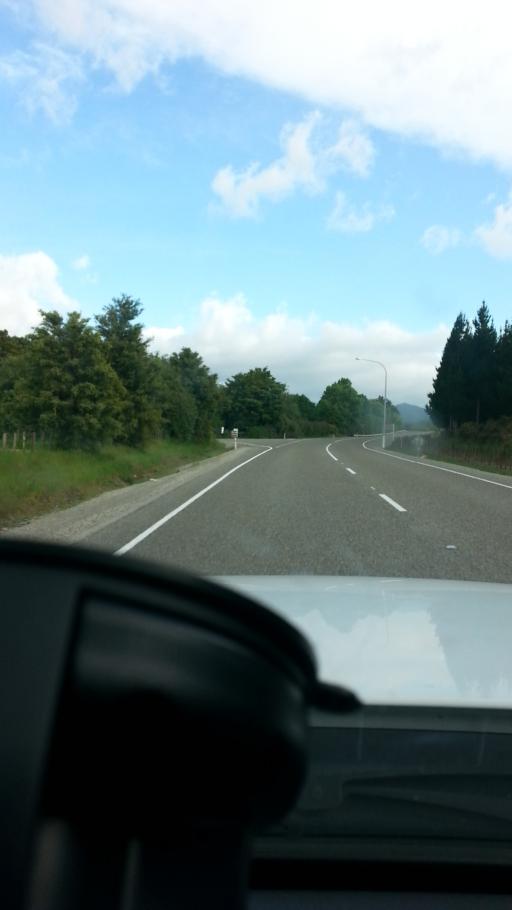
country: NZ
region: Wellington
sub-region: Masterton District
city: Masterton
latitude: -40.8103
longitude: 175.6209
